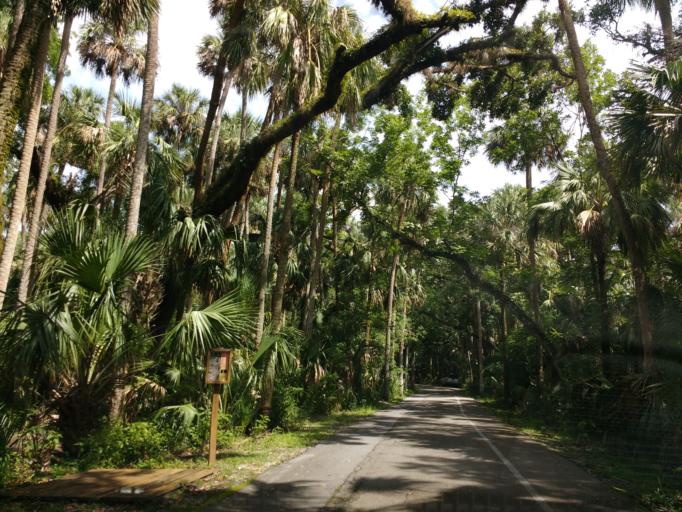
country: US
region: Florida
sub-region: Highlands County
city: Sebring
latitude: 27.4732
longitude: -81.5519
